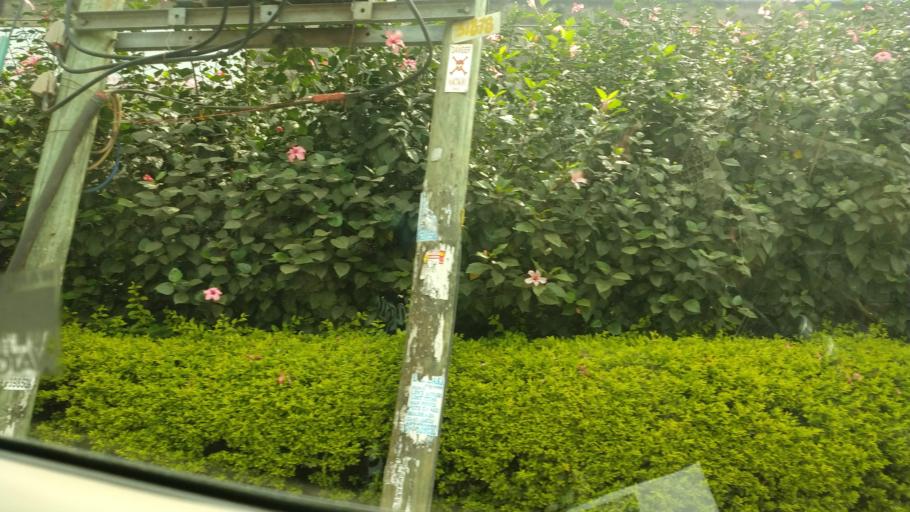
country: KE
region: Nairobi Area
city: Nairobi
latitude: -1.2952
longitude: 36.7792
